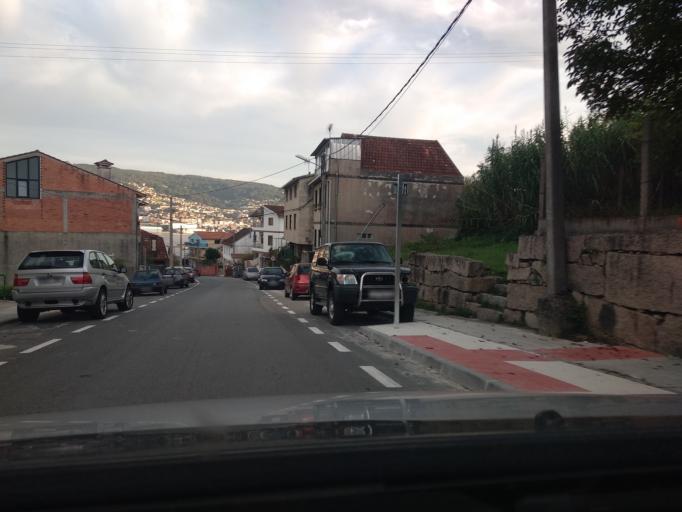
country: ES
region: Galicia
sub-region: Provincia de Pontevedra
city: Moana
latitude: 42.2878
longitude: -8.6857
